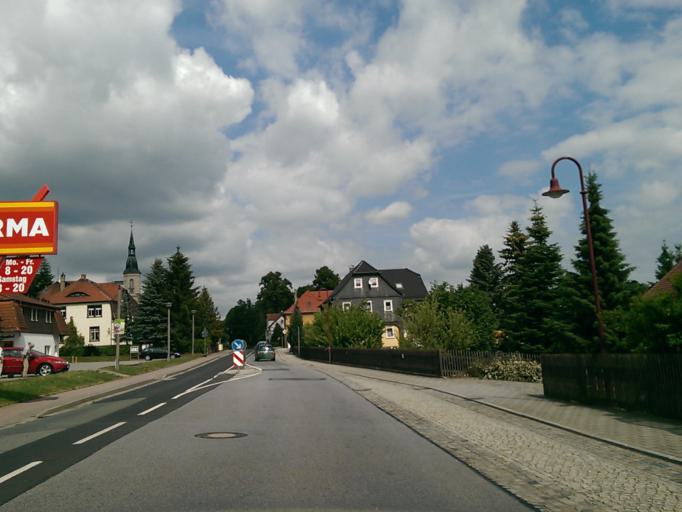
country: DE
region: Saxony
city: Eibau
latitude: 50.9701
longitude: 14.7052
